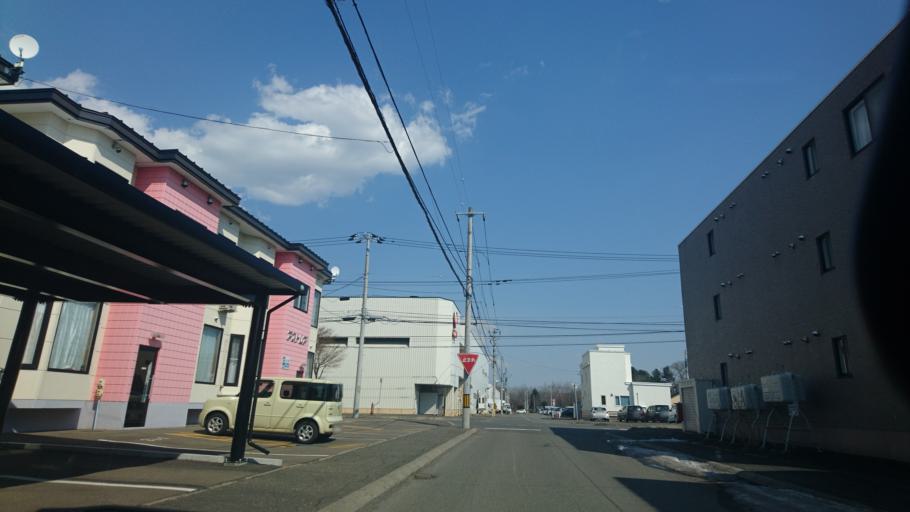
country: JP
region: Hokkaido
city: Obihiro
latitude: 42.9150
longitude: 143.1238
